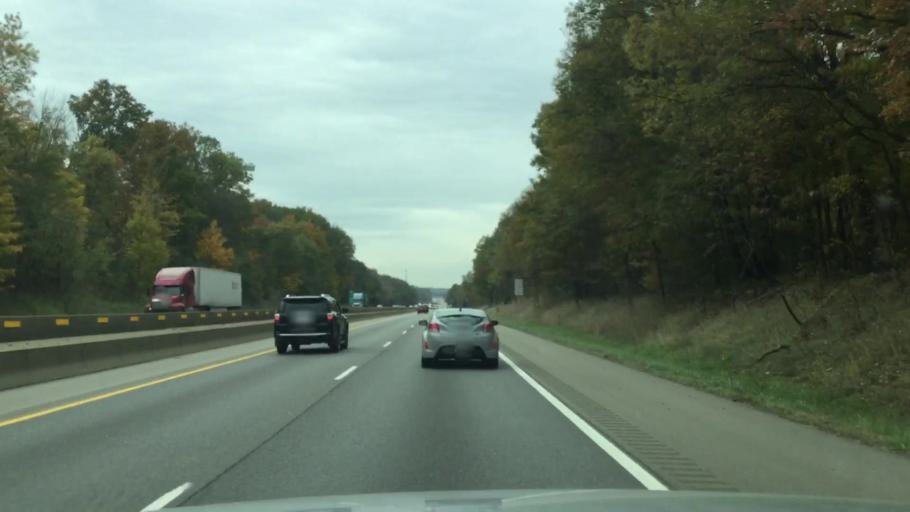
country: US
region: Michigan
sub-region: Kalamazoo County
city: Galesburg
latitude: 42.2807
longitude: -85.3882
